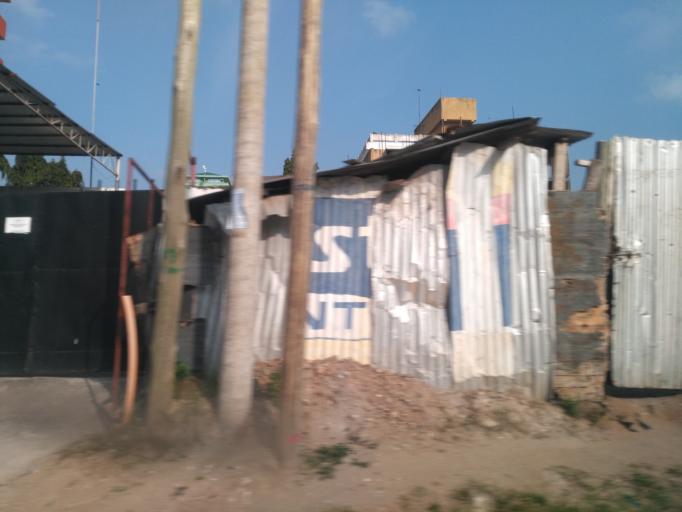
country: TZ
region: Dar es Salaam
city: Dar es Salaam
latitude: -6.8124
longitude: 39.2772
